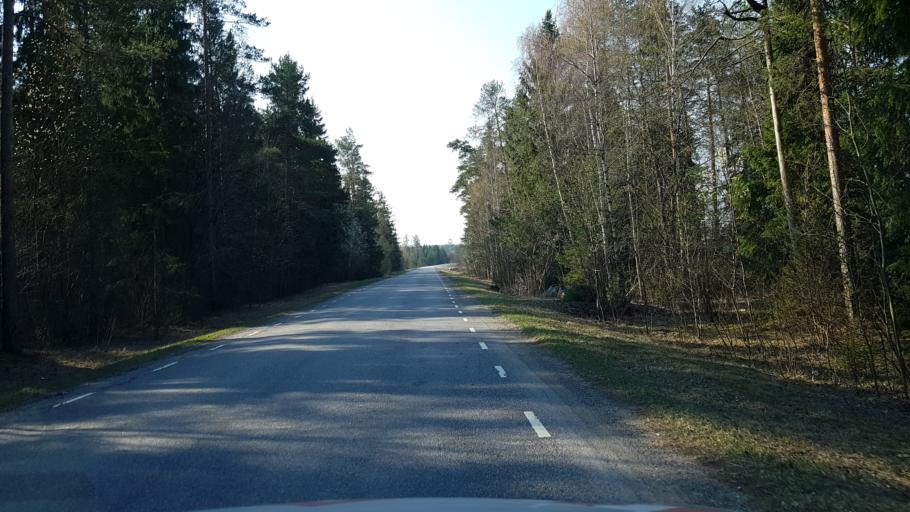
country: EE
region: Raplamaa
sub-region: Kohila vald
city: Kohila
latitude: 59.1896
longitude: 24.6617
